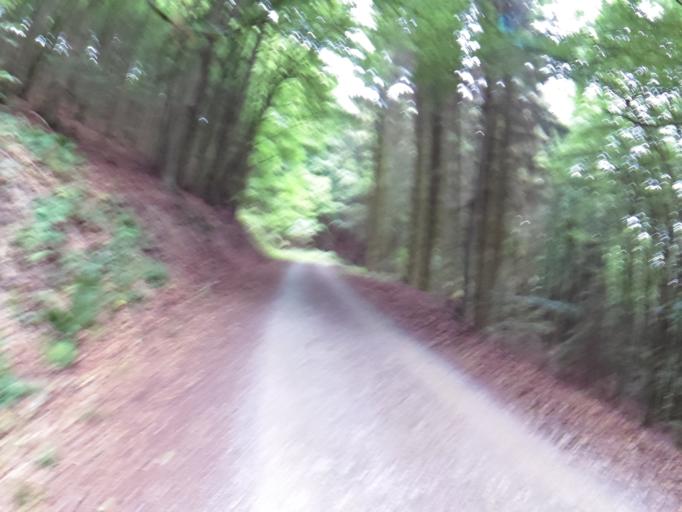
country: DE
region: North Rhine-Westphalia
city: Heimbach
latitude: 50.6241
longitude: 6.4033
